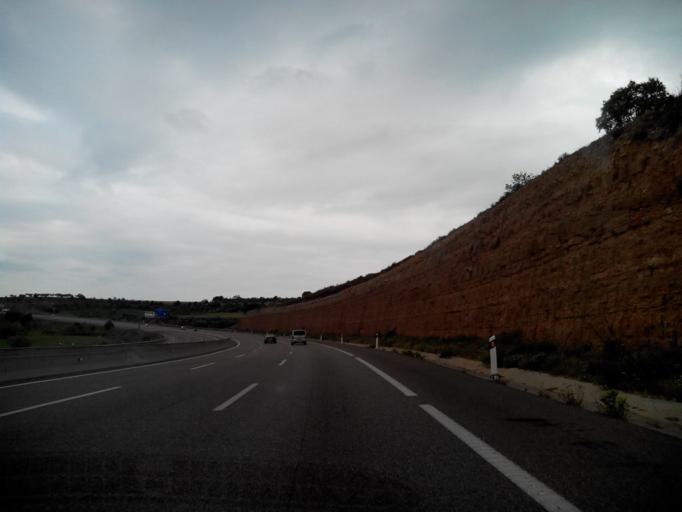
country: ES
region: Catalonia
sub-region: Provincia de Lleida
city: Cervera
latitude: 41.6870
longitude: 1.2657
